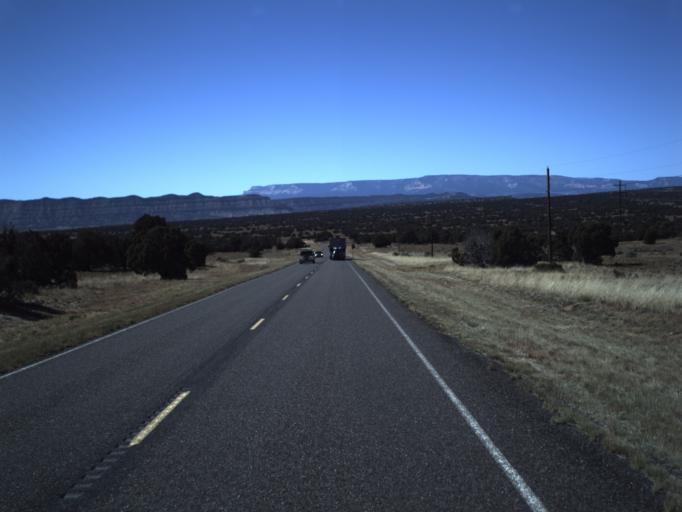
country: US
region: Utah
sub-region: Wayne County
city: Loa
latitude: 37.7495
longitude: -111.4818
